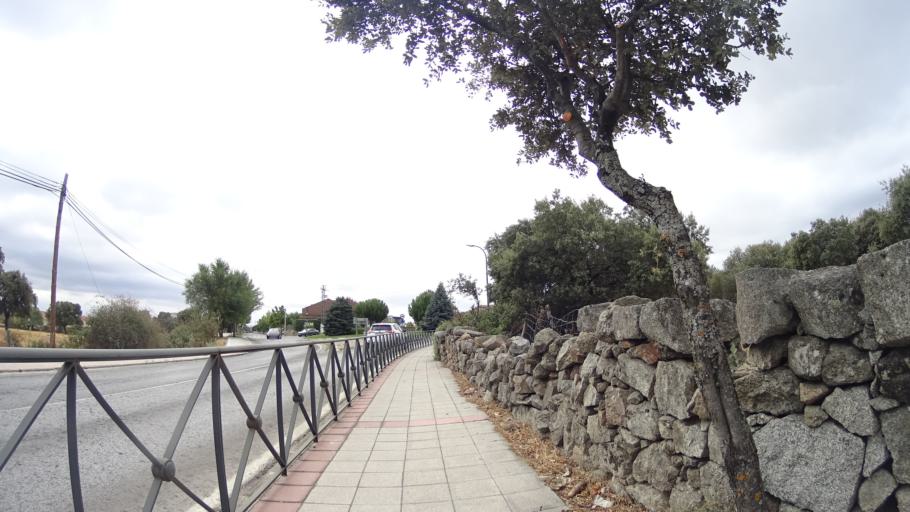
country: ES
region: Madrid
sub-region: Provincia de Madrid
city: Galapagar
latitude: 40.5856
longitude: -4.0117
